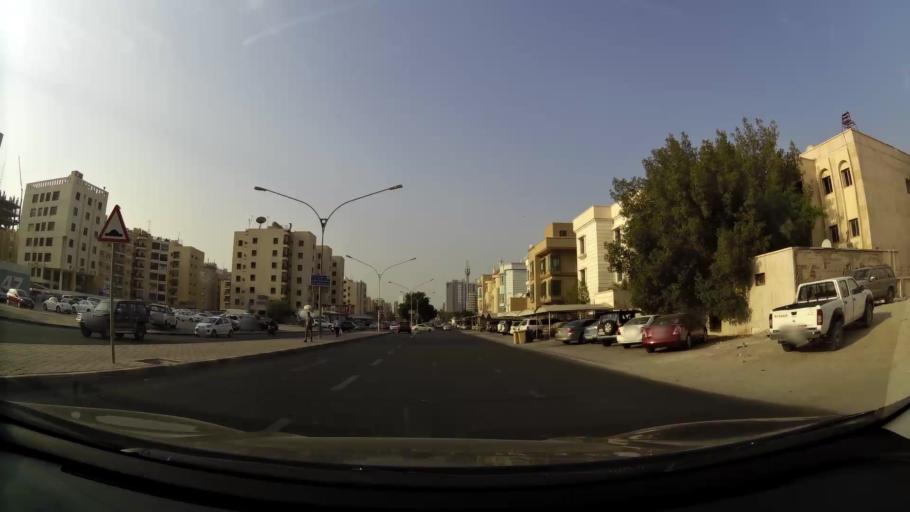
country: KW
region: Muhafazat Hawalli
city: Hawalli
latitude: 29.3221
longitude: 48.0317
